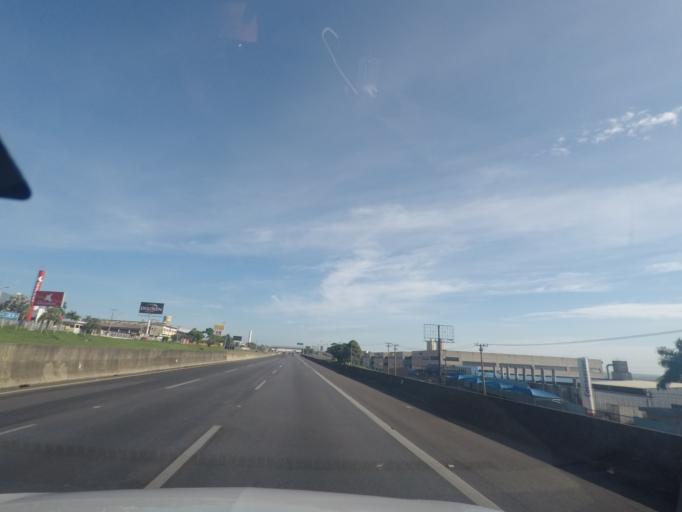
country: BR
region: Sao Paulo
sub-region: Americana
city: Americana
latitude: -22.7250
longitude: -47.2929
